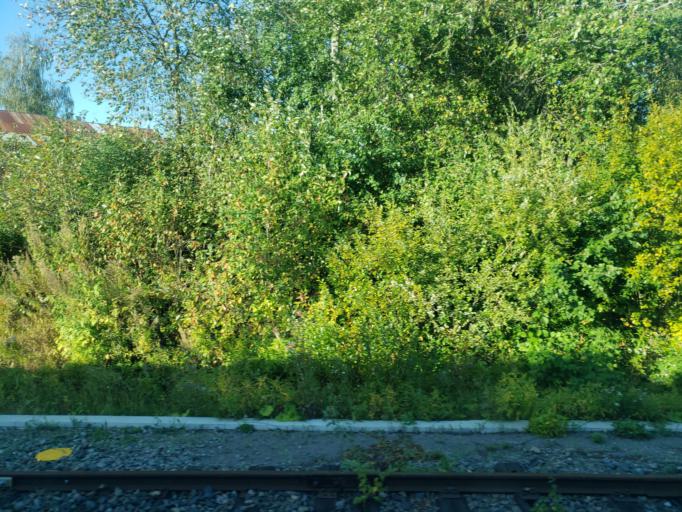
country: FI
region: South Karelia
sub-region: Lappeenranta
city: Lappeenranta
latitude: 60.8682
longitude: 28.2868
